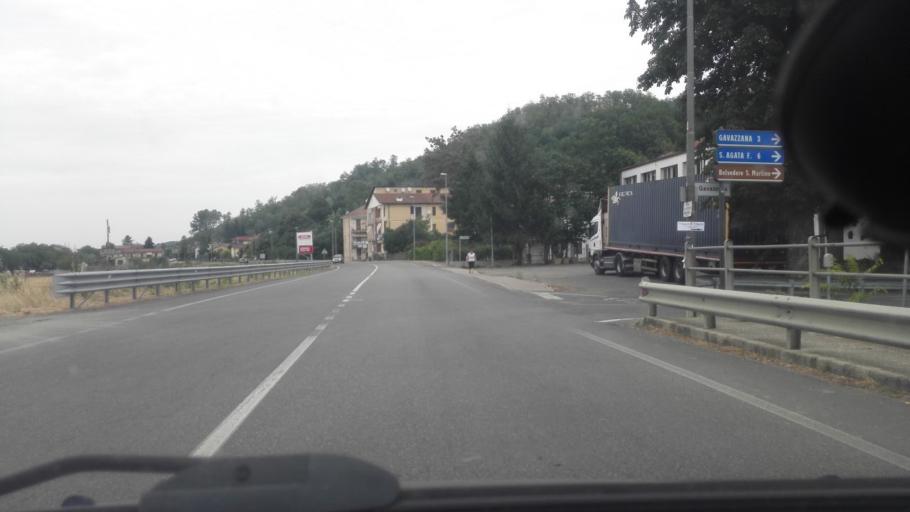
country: IT
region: Piedmont
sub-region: Provincia di Alessandria
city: Cassano Spinola
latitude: 44.7693
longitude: 8.8654
